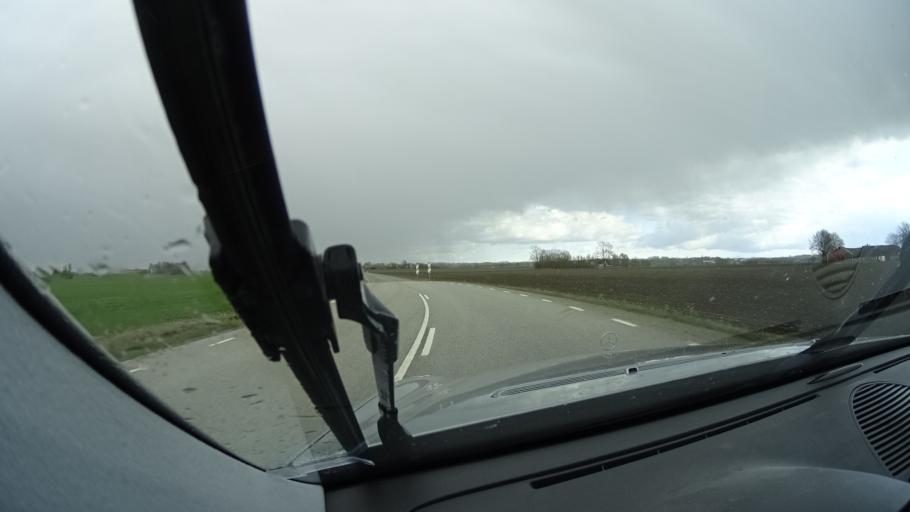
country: SE
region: Skane
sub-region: Lunds Kommun
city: Lund
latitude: 55.7451
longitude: 13.1524
